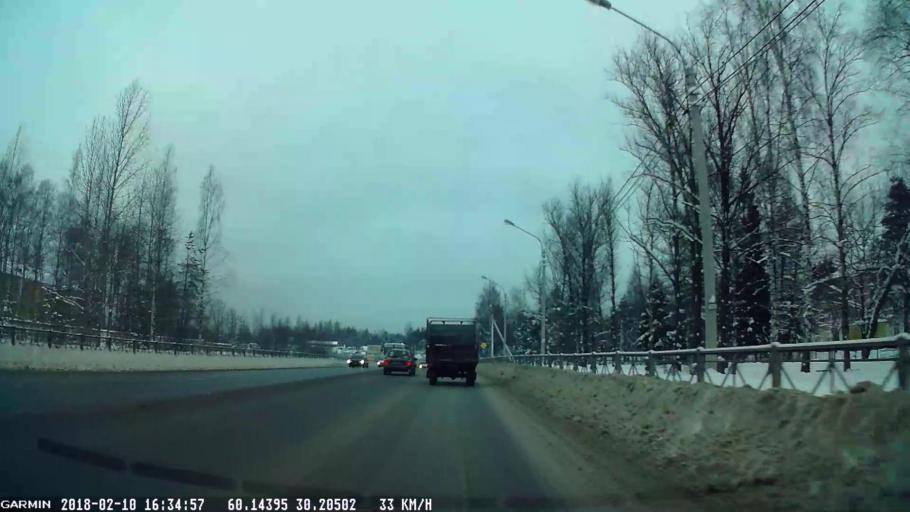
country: RU
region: Leningrad
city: Sertolovo
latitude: 60.1447
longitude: 30.2041
